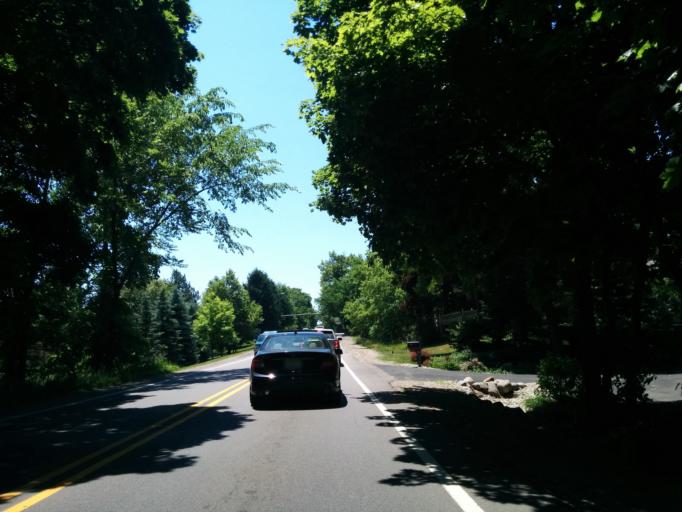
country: US
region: Michigan
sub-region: Oakland County
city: Orchard Lake
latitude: 42.5754
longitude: -83.3705
